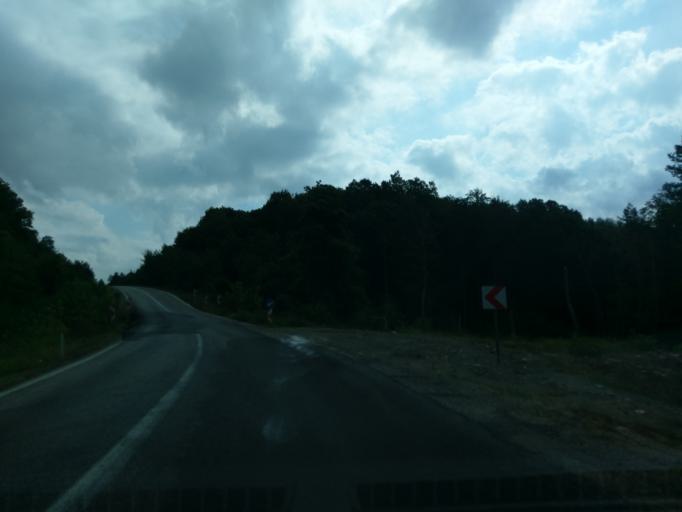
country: TR
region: Sinop
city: Yenikonak
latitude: 41.9456
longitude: 34.7494
